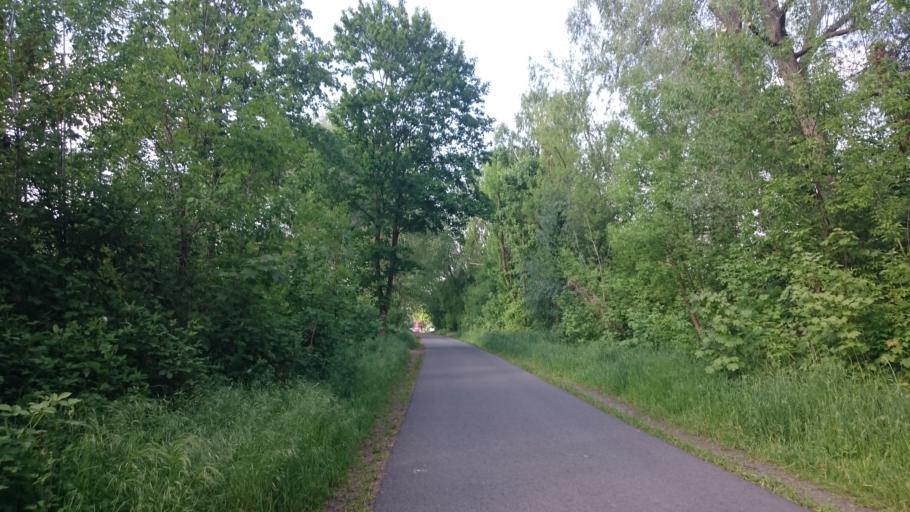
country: DE
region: Brandenburg
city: Wildau
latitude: 52.3193
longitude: 13.6364
